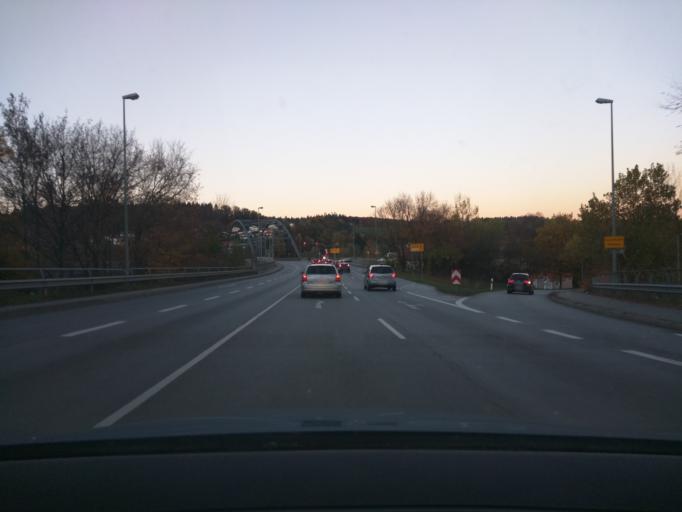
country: DE
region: Bavaria
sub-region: Lower Bavaria
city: Passau
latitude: 48.5745
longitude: 13.4127
